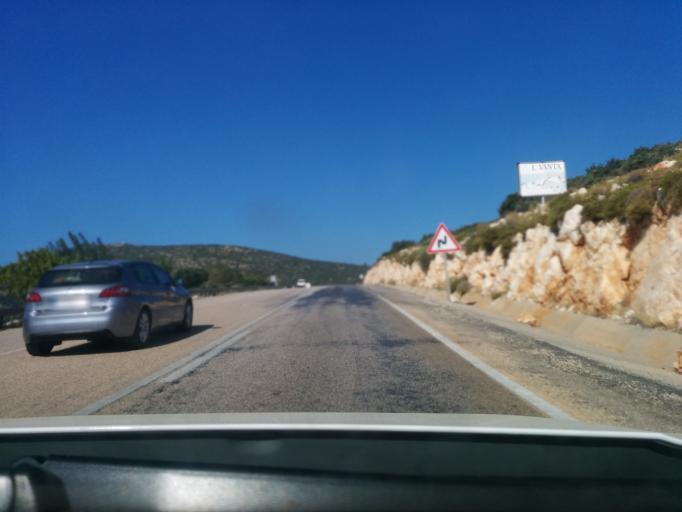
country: TR
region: Antalya
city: Kalkan
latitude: 36.2706
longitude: 29.3983
